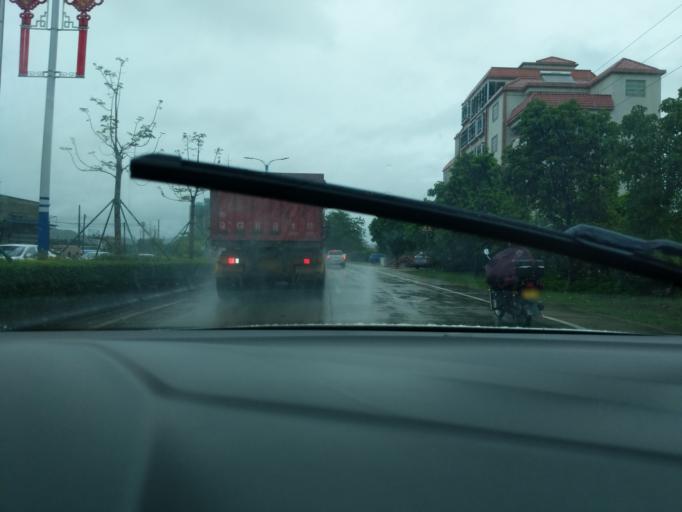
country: CN
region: Guangdong
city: Pingshi
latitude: 22.2089
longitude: 112.3250
